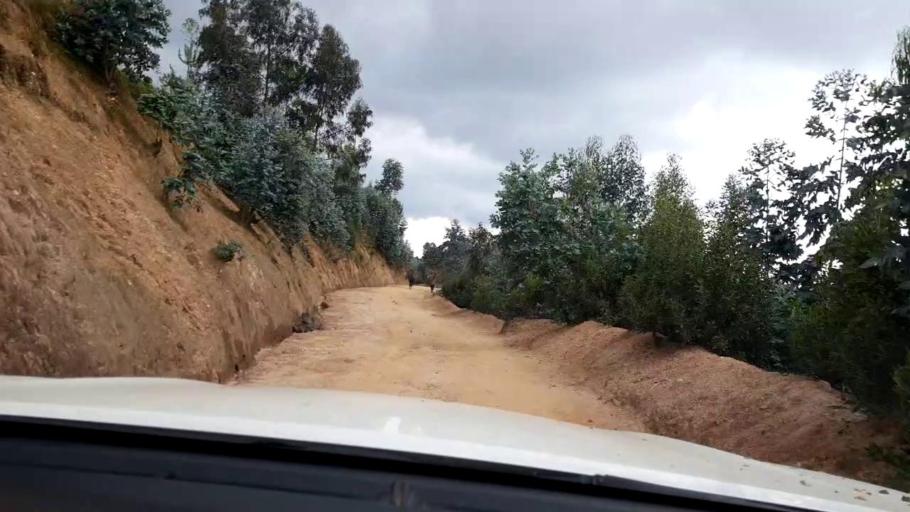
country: RW
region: Western Province
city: Kibuye
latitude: -1.8954
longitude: 29.5282
